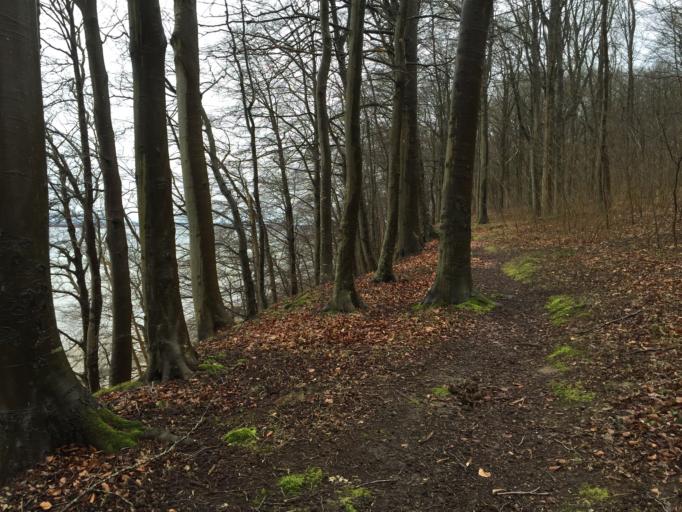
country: DK
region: South Denmark
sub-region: Assens Kommune
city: Harby
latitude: 55.1414
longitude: 10.0326
